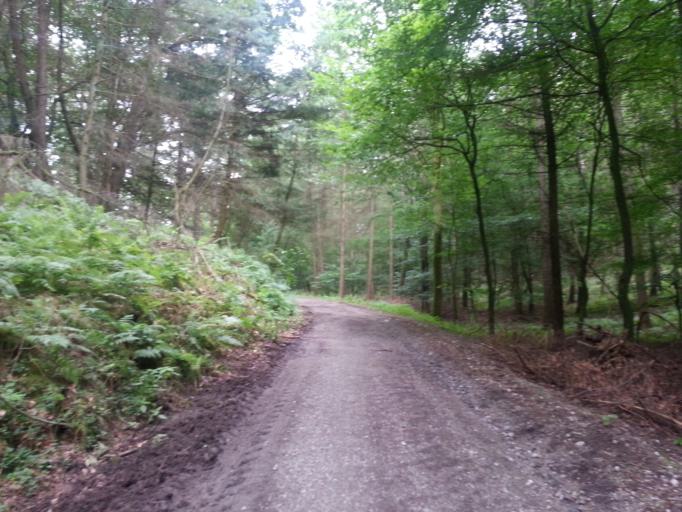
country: DE
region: North Rhine-Westphalia
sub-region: Regierungsbezirk Munster
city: Haltern
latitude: 51.7043
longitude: 7.2170
